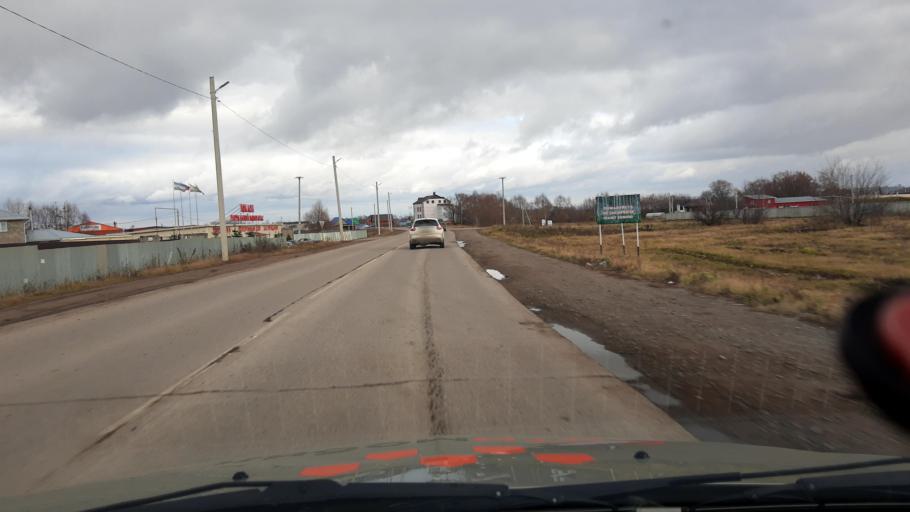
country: RU
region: Bashkortostan
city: Mikhaylovka
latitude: 54.8011
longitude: 55.8736
